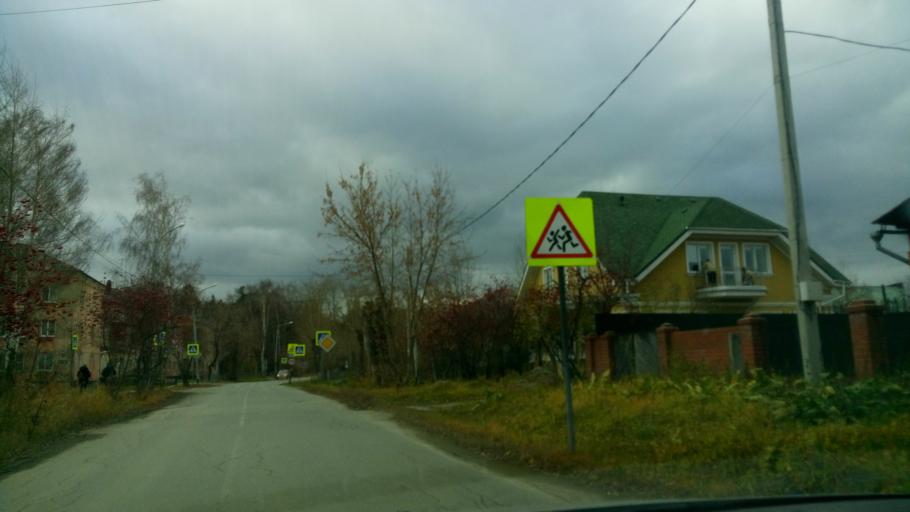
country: RU
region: Sverdlovsk
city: Sredneuralsk
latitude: 56.9906
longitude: 60.4721
